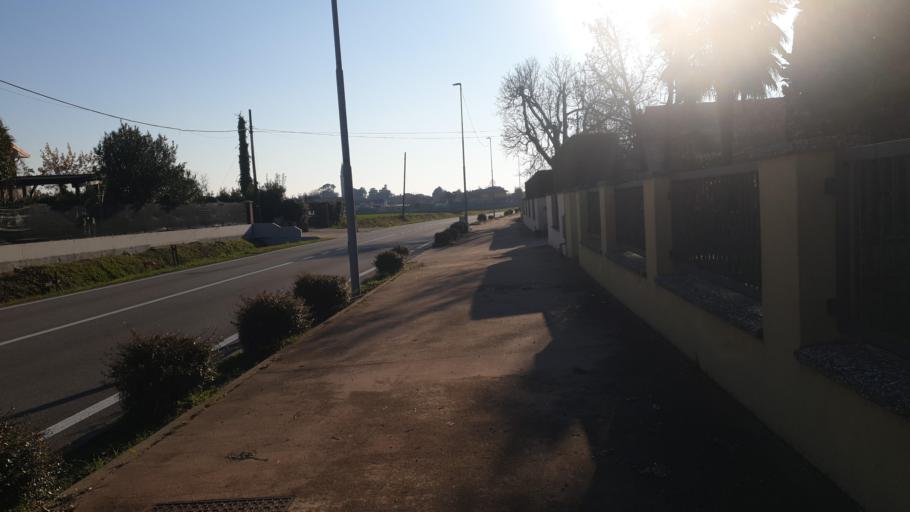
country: IT
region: Veneto
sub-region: Provincia di Padova
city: Carrara San Giorgio
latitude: 45.2996
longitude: 11.8200
